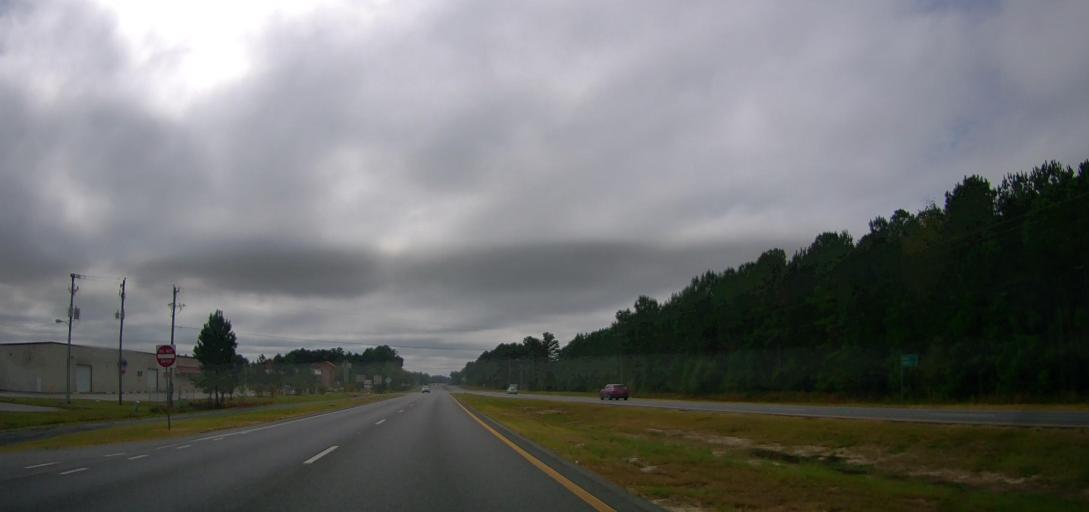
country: US
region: Georgia
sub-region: Colquitt County
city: Moultrie
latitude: 31.1145
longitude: -83.7856
